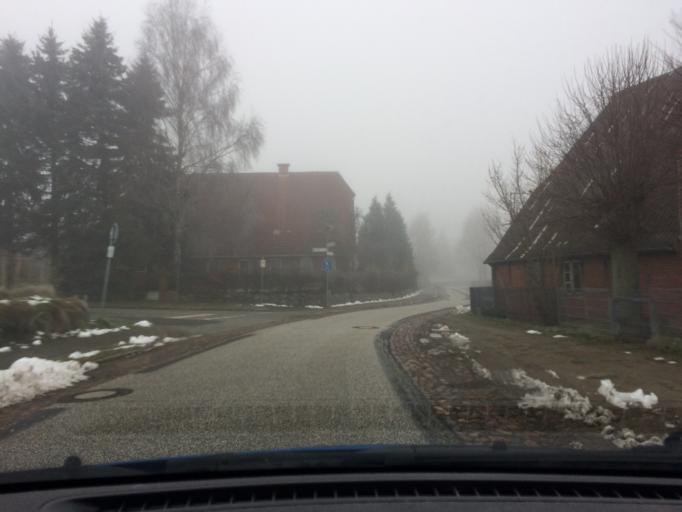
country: DE
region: Schleswig-Holstein
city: Juliusburg
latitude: 53.4151
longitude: 10.5051
